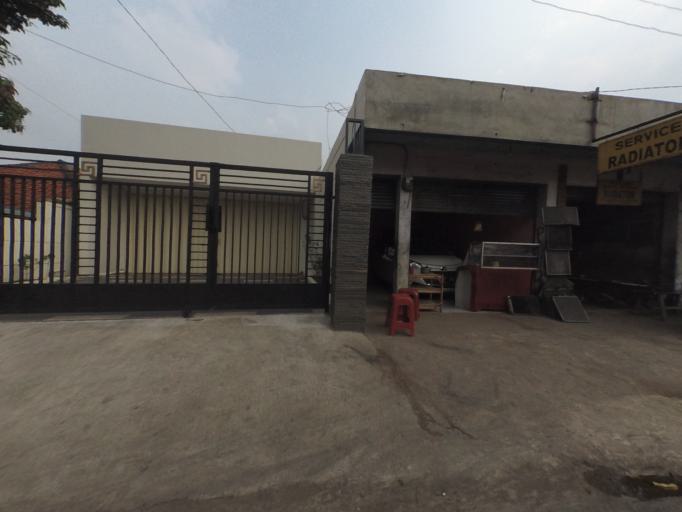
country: ID
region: West Java
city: Ciampea
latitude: -6.5574
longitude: 106.6930
